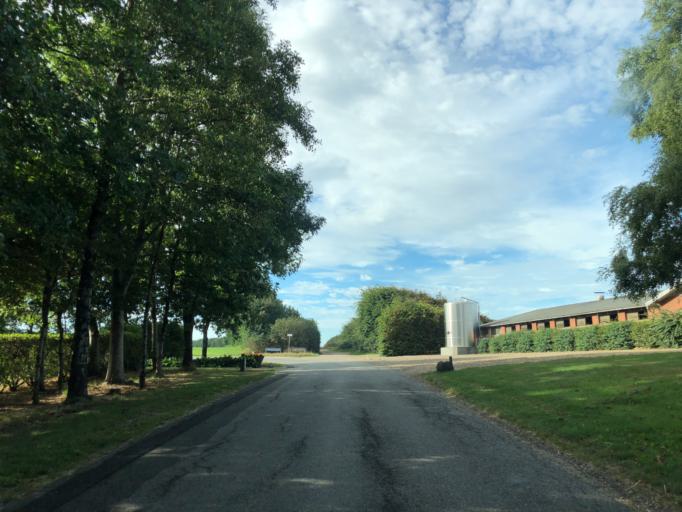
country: DK
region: Central Jutland
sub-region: Holstebro Kommune
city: Ulfborg
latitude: 56.1383
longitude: 8.4051
